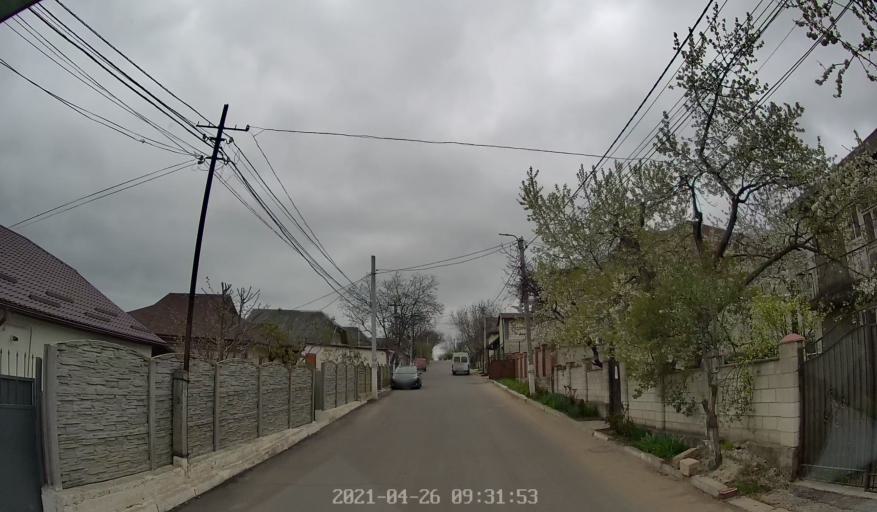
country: MD
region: Chisinau
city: Stauceni
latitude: 47.0938
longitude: 28.8695
